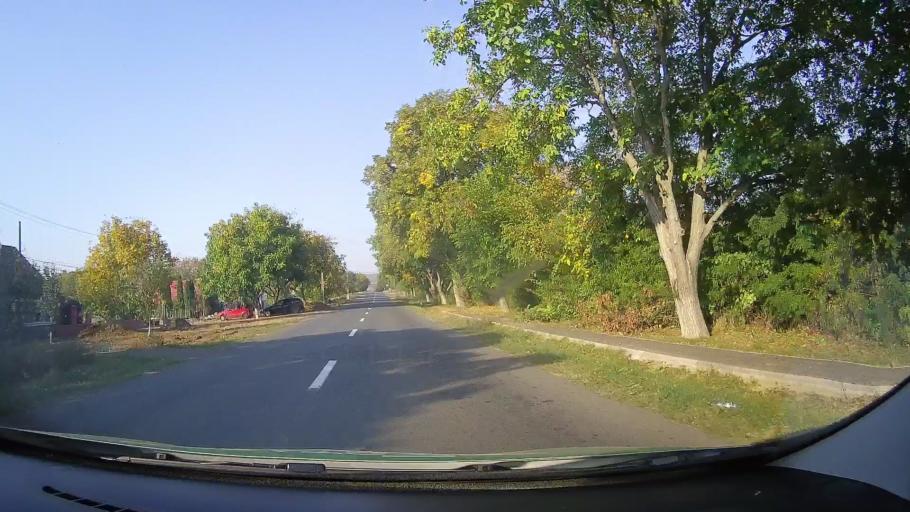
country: RO
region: Arad
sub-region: Comuna Paulis
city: Paulis
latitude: 46.1249
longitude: 21.5989
